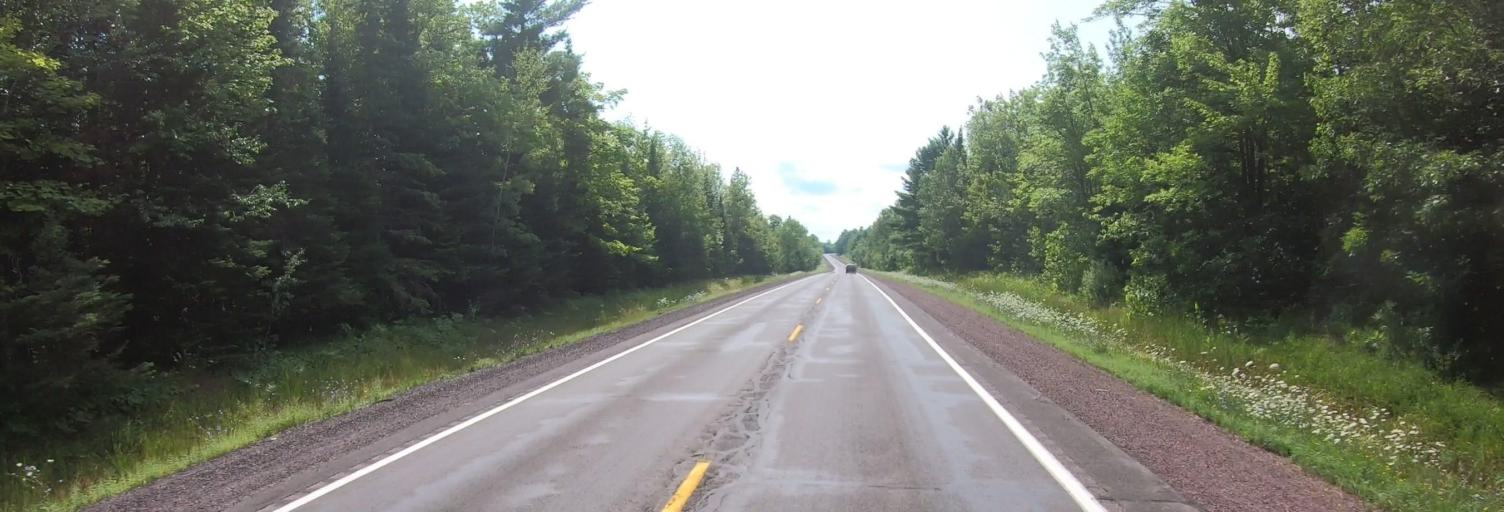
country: US
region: Michigan
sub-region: Ontonagon County
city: Ontonagon
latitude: 46.7335
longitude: -89.1259
